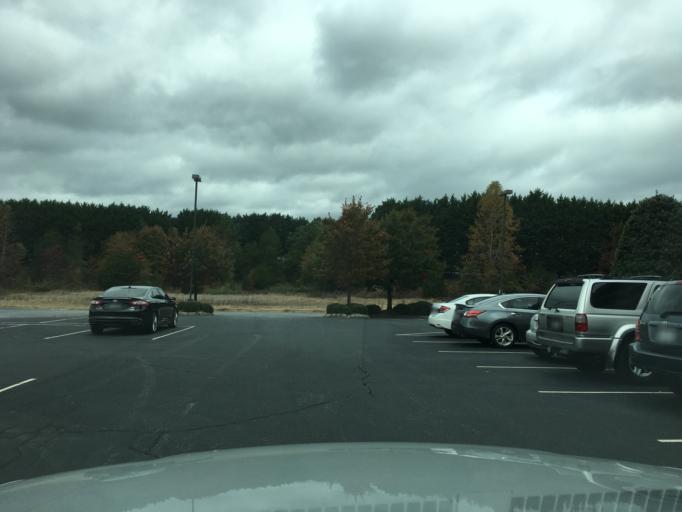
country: US
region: North Carolina
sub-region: Catawba County
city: Hickory
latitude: 35.7019
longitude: -81.2991
